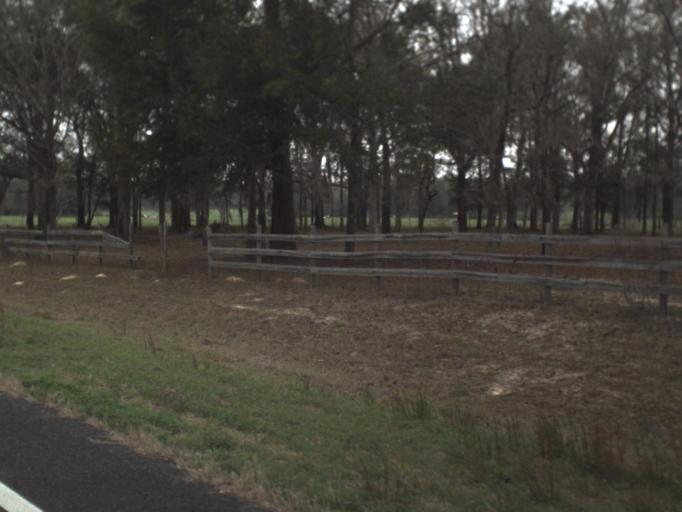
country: US
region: Florida
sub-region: Jefferson County
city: Monticello
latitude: 30.4085
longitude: -83.9786
